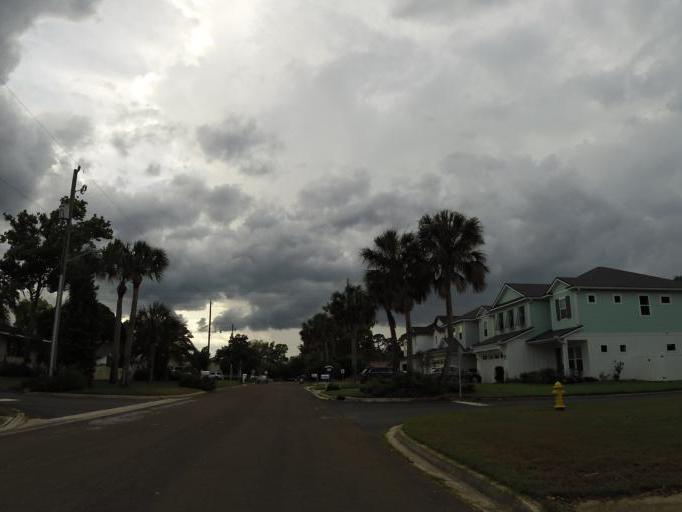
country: US
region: Florida
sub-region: Duval County
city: Jacksonville Beach
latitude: 30.2734
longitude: -81.3943
